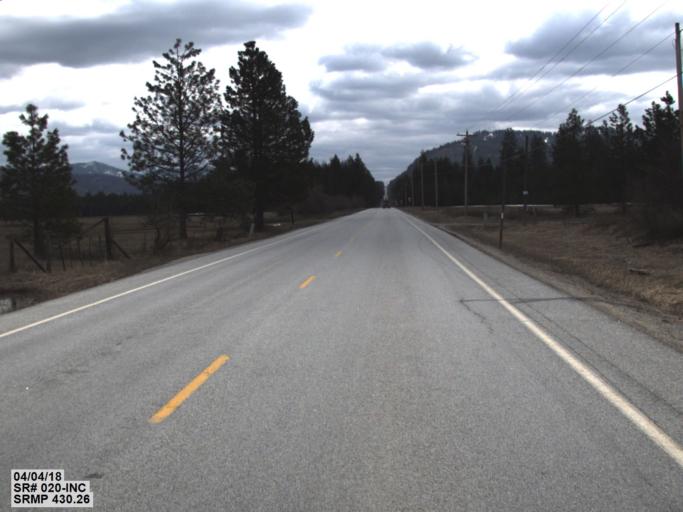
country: US
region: Washington
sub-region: Pend Oreille County
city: Newport
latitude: 48.2297
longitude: -117.1565
